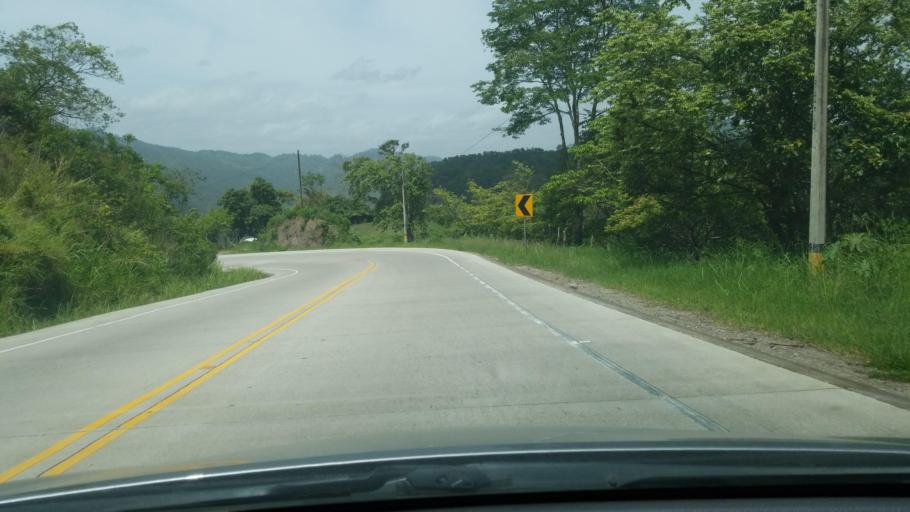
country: HN
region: Copan
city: Veracruz
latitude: 14.9124
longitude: -88.7540
